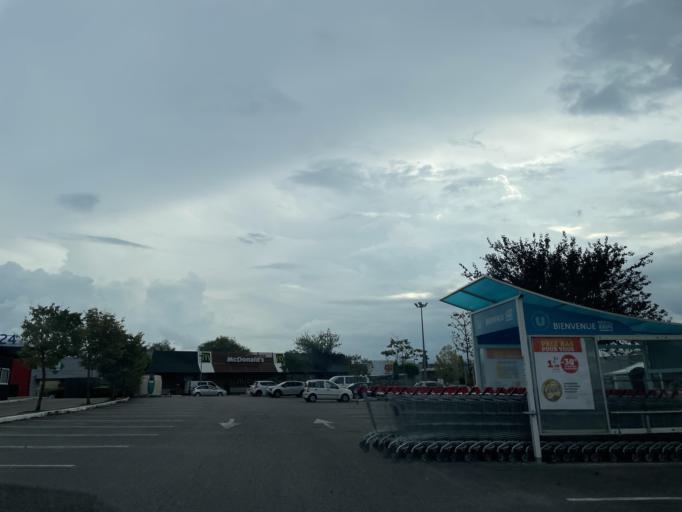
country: FR
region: Haute-Normandie
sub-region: Departement de la Seine-Maritime
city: Gournay-en-Bray
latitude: 49.4786
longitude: 1.7396
